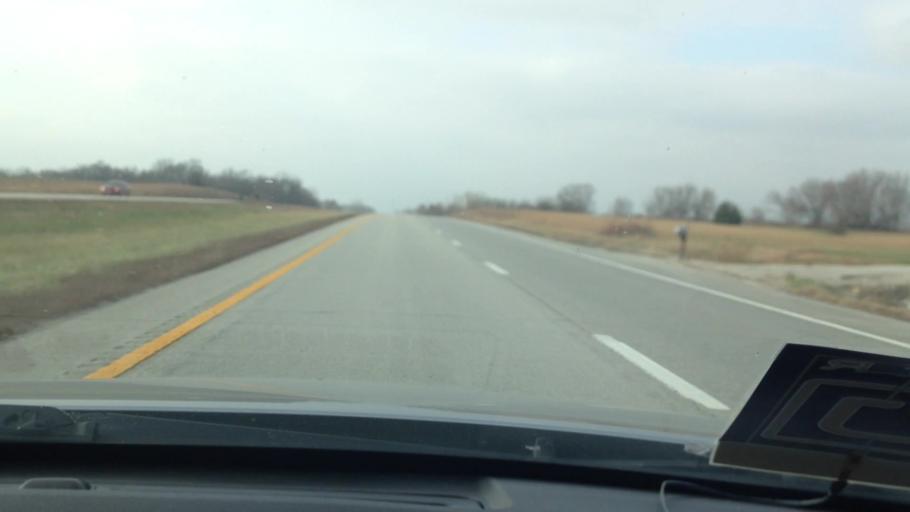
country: US
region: Missouri
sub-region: Cass County
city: Garden City
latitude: 38.5309
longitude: -94.1506
